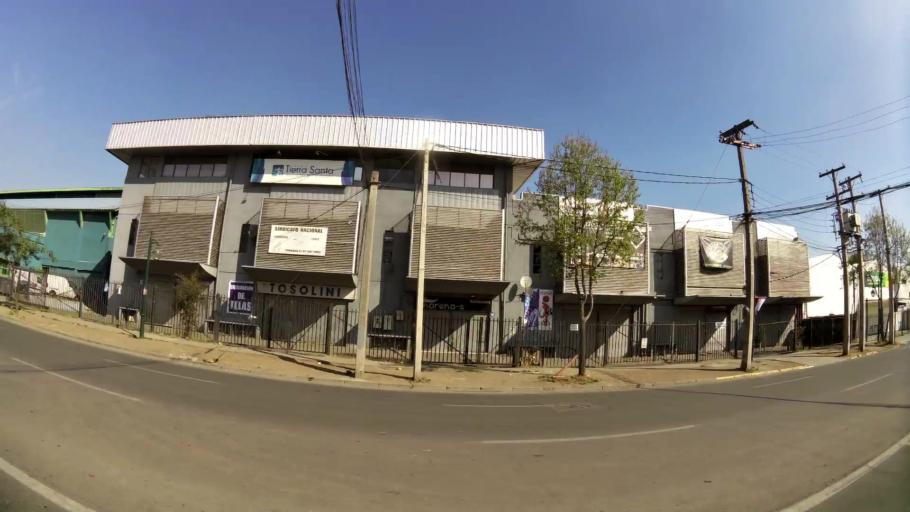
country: CL
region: Santiago Metropolitan
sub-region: Provincia de Santiago
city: Santiago
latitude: -33.4711
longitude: -70.6212
